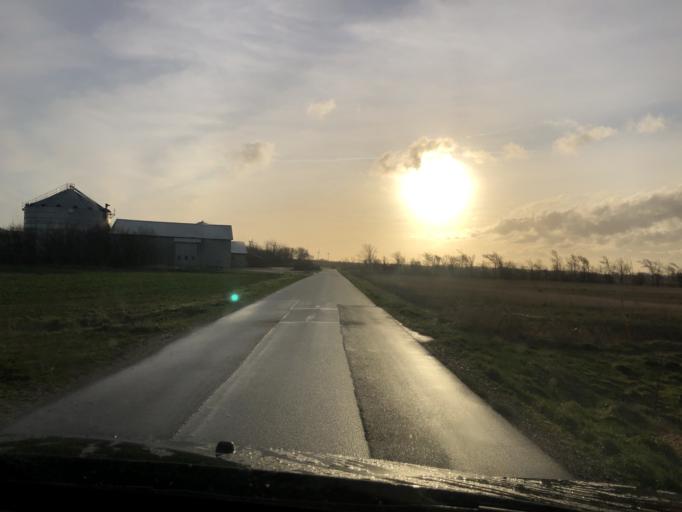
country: DK
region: Central Jutland
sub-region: Ringkobing-Skjern Kommune
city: Skjern
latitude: 55.8625
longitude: 8.3737
